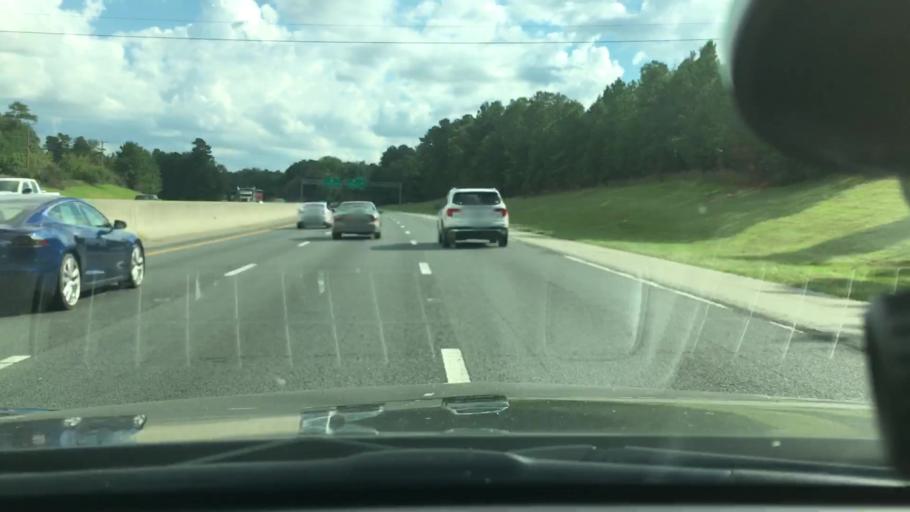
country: US
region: North Carolina
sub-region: Orange County
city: Chapel Hill
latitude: 35.9183
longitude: -78.9851
